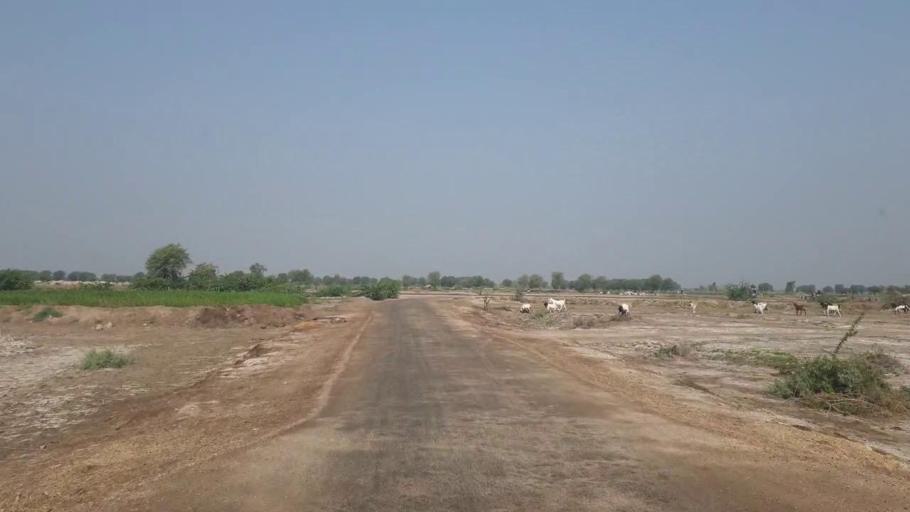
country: PK
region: Sindh
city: Umarkot
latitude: 25.4129
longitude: 69.6829
